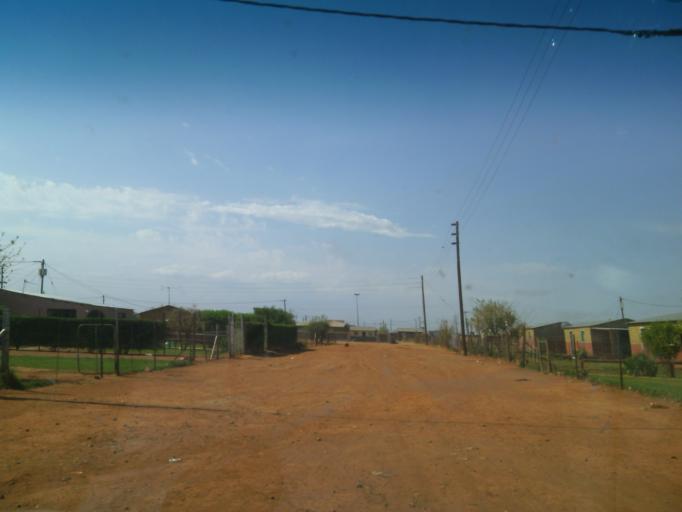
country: ZA
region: Northern Cape
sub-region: Frances Baard District Municipality
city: Barkly West
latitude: -28.5213
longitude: 24.5025
